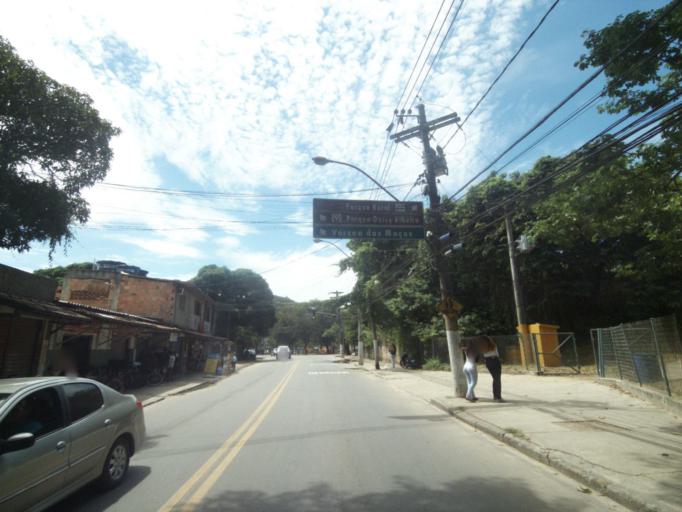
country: BR
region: Rio de Janeiro
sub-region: Niteroi
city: Niteroi
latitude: -22.9353
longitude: -43.0100
